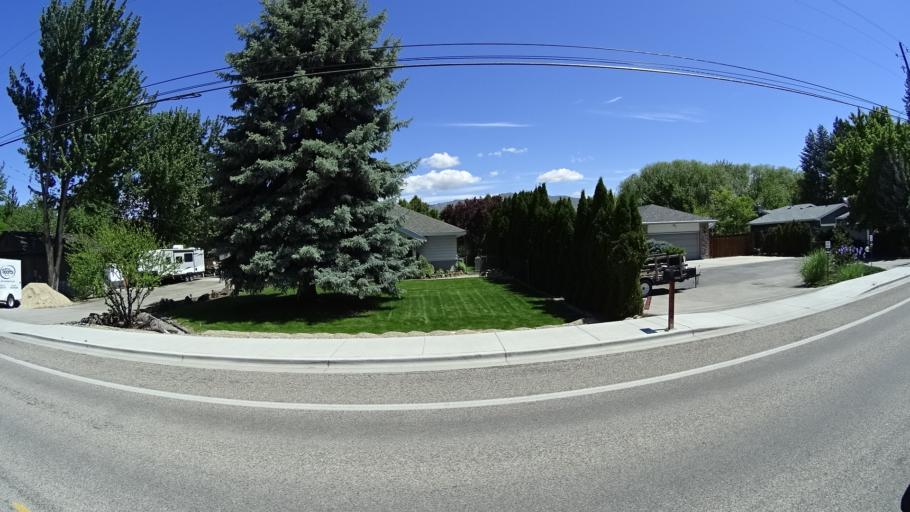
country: US
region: Idaho
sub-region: Ada County
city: Boise
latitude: 43.5673
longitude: -116.1481
